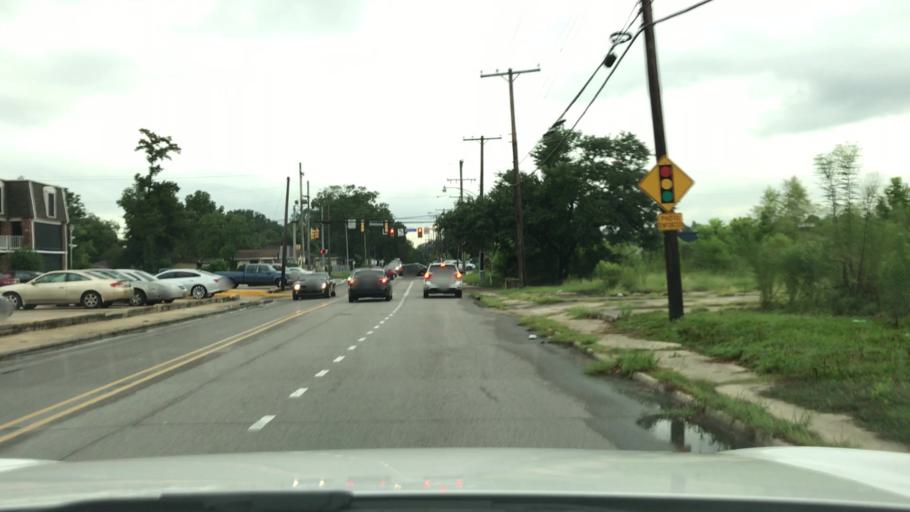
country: US
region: Louisiana
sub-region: East Baton Rouge Parish
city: Merrydale
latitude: 30.4789
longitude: -91.1175
